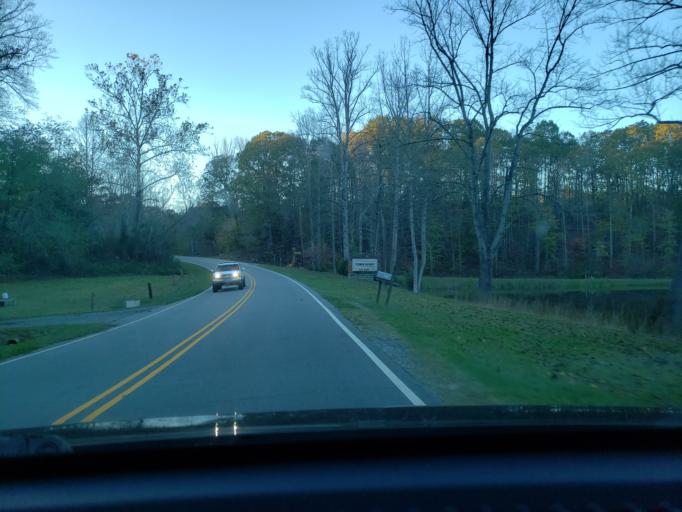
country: US
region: North Carolina
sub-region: Stokes County
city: Danbury
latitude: 36.3920
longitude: -80.1927
